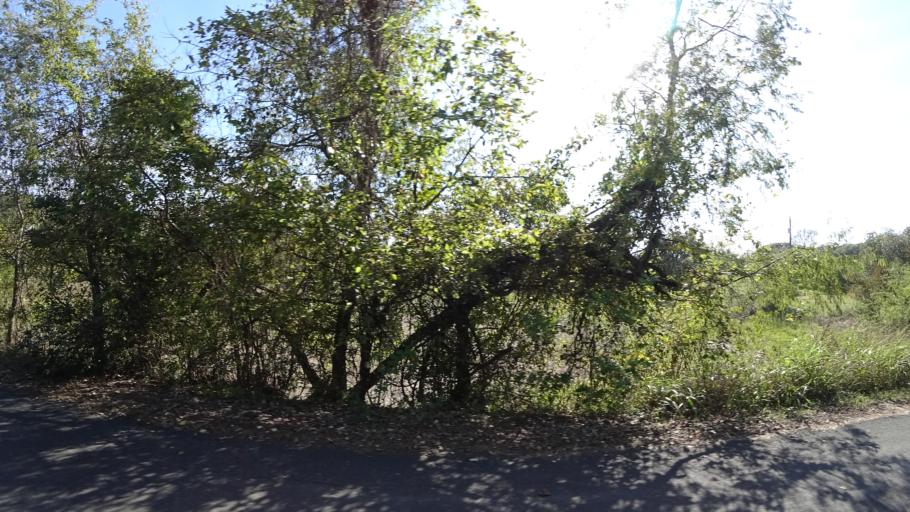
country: US
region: Texas
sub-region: Travis County
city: Bee Cave
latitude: 30.2347
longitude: -97.9356
